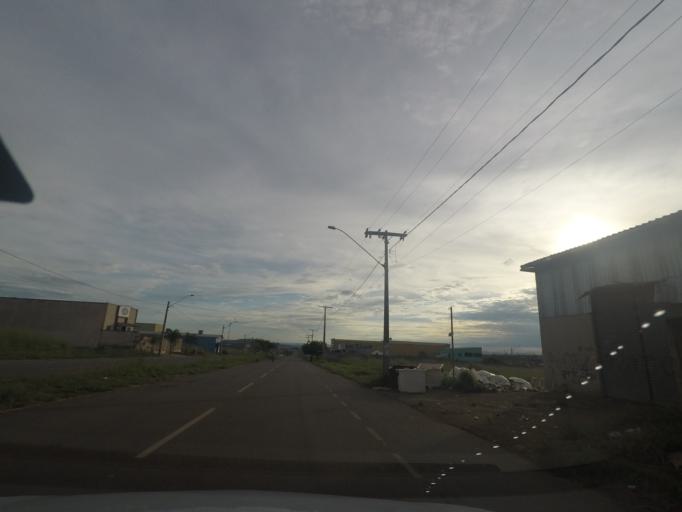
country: BR
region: Goias
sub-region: Trindade
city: Trindade
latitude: -16.7285
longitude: -49.4089
